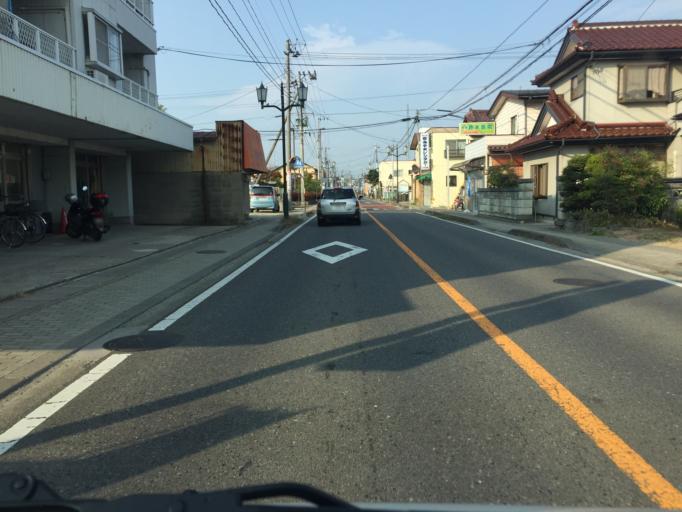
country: JP
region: Fukushima
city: Koriyama
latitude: 37.4183
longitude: 140.3912
